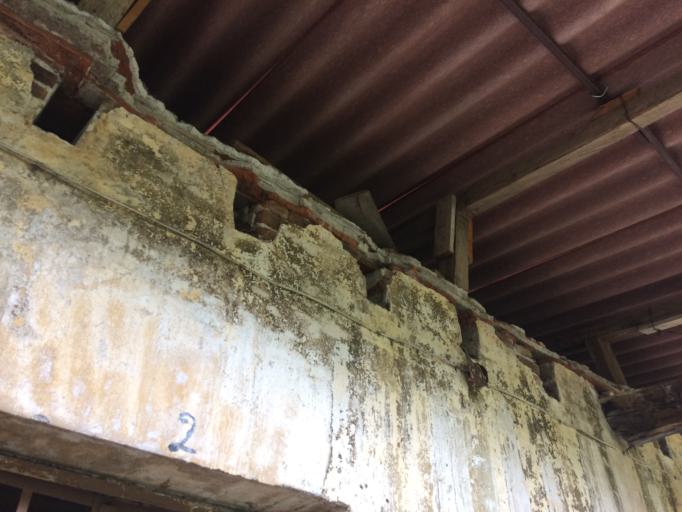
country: MX
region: Mexico
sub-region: Ocuilan
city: Plaza Nueva
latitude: 18.9384
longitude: -99.4242
